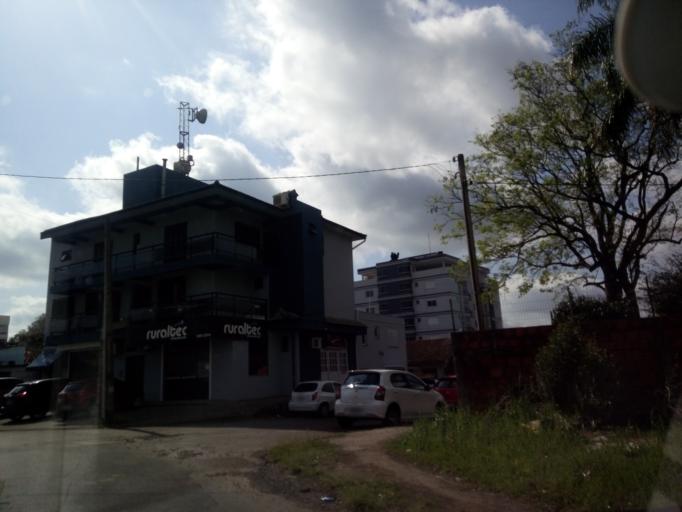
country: BR
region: Rio Grande do Sul
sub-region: Santa Maria
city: Santa Maria
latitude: -29.7024
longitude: -53.7127
